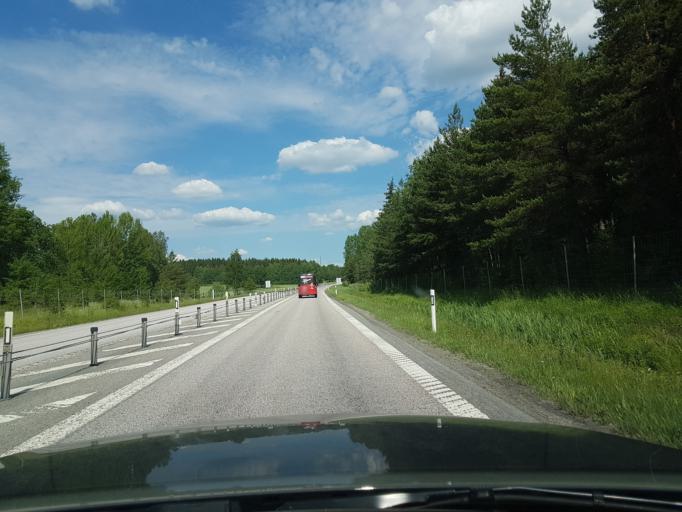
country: SE
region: Stockholm
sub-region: Vallentuna Kommun
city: Vallentuna
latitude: 59.5151
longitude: 18.1778
